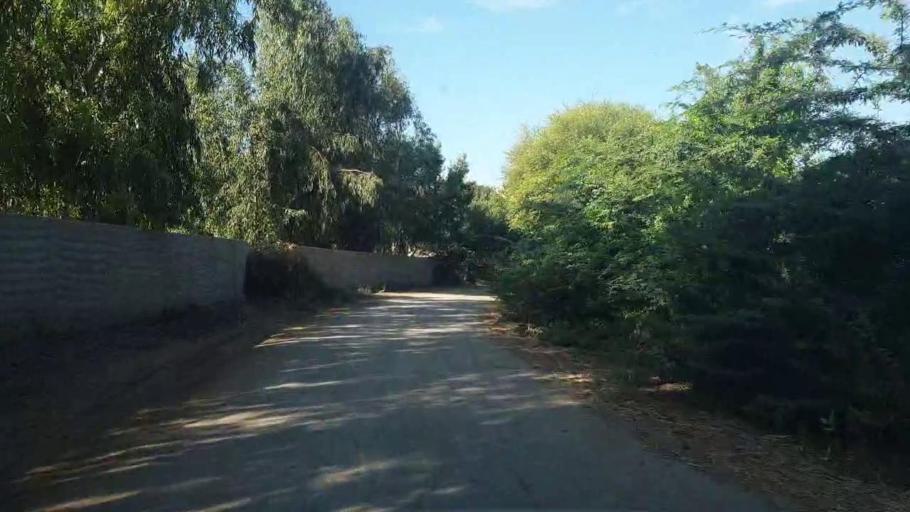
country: PK
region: Sindh
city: Talhar
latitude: 24.8900
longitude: 68.8157
